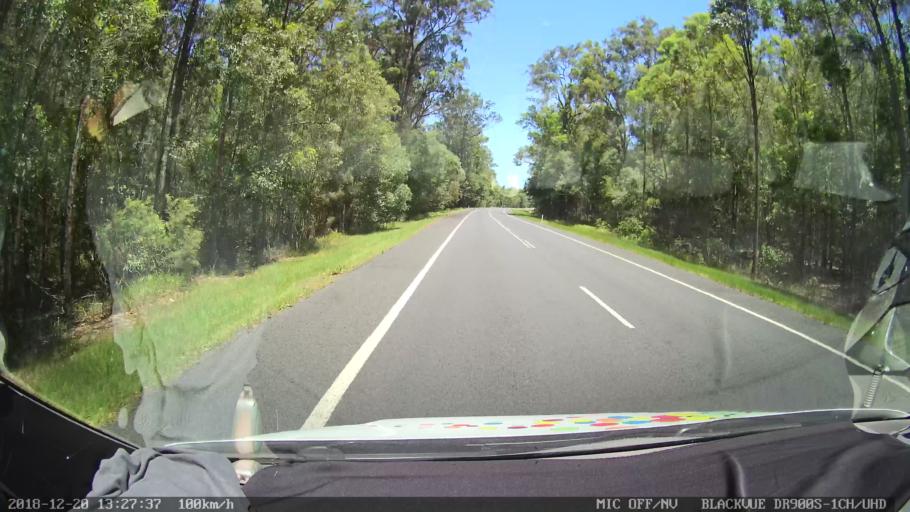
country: AU
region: New South Wales
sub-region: Clarence Valley
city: Gordon
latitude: -29.1626
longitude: 152.9926
